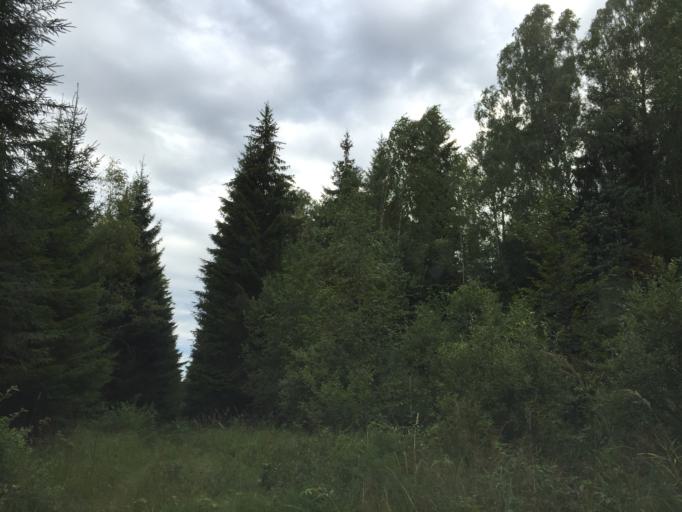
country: LV
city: Tireli
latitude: 56.8450
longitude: 23.6746
